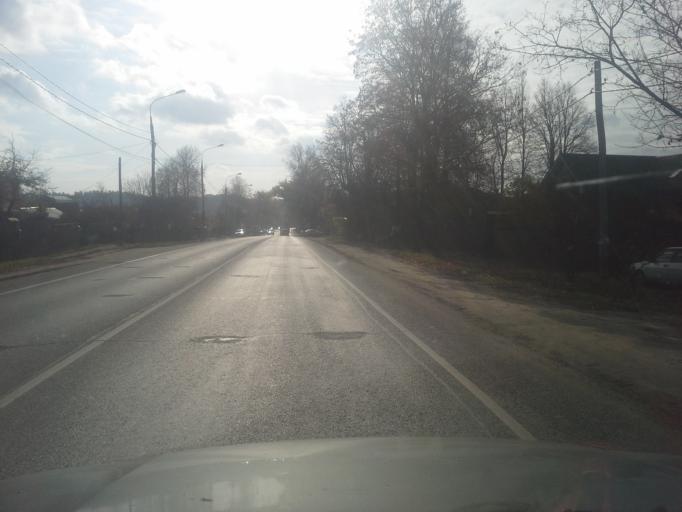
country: RU
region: Moskovskaya
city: Zvenigorod
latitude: 55.7211
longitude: 36.8642
